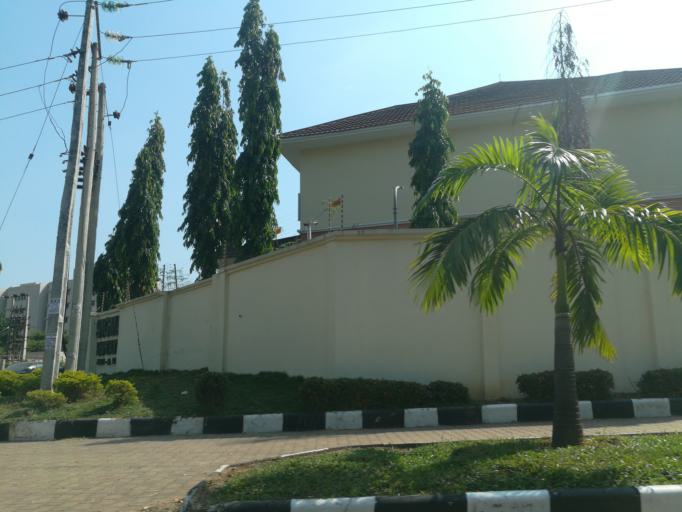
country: NG
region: Abuja Federal Capital Territory
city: Abuja
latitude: 9.0643
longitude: 7.4300
